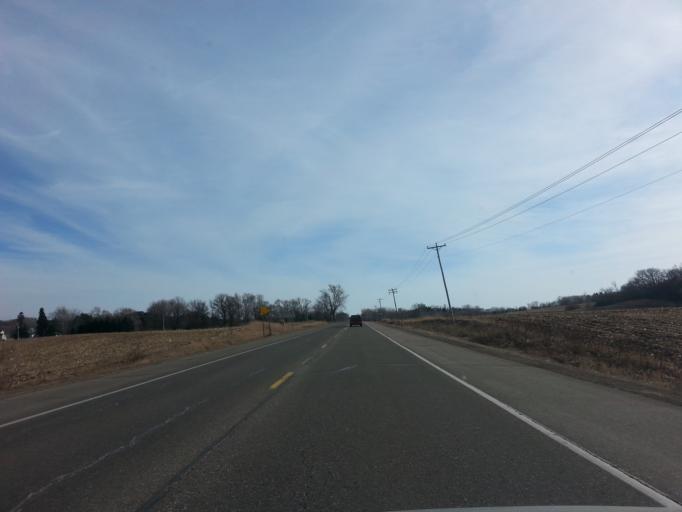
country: US
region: Minnesota
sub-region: Washington County
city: Lake Elmo
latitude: 44.9189
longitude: -92.8626
